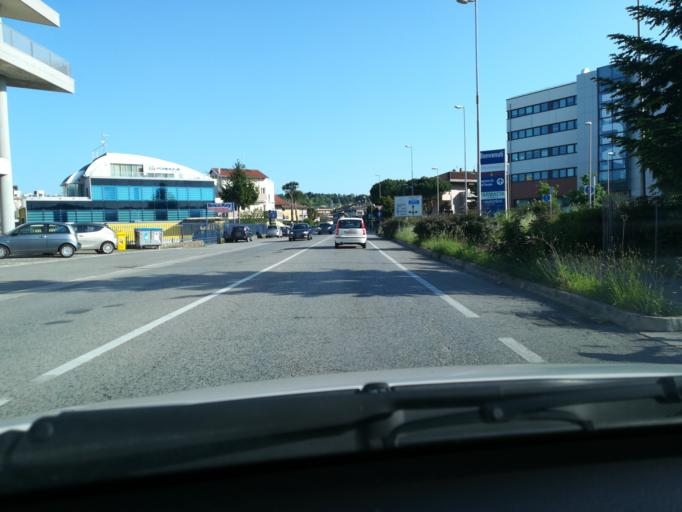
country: IT
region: Emilia-Romagna
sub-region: Provincia di Rimini
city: Riccione
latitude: 43.9970
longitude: 12.6482
